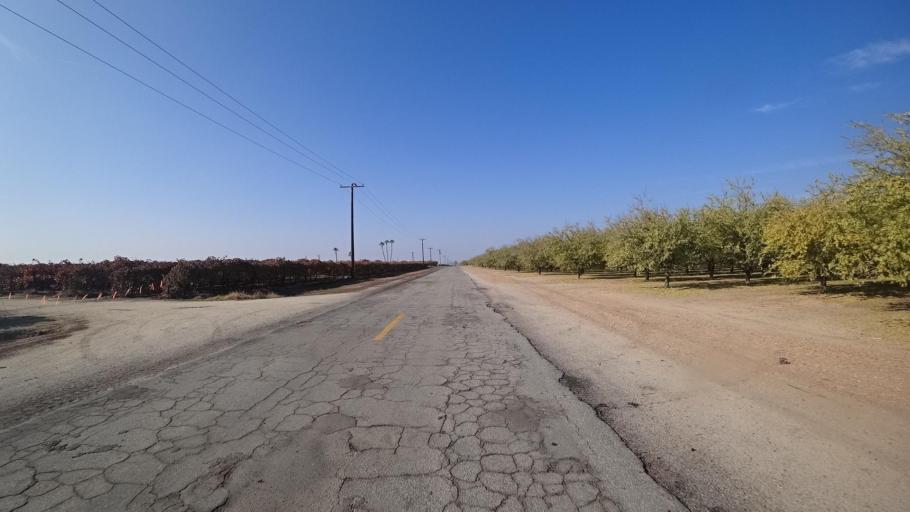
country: US
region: California
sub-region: Kern County
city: McFarland
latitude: 35.6891
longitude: -119.1666
